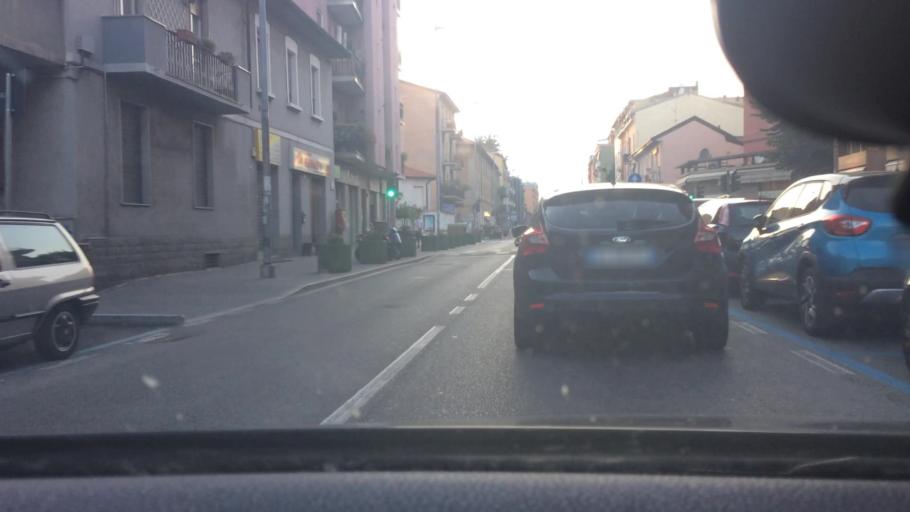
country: IT
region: Lombardy
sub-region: Citta metropolitana di Milano
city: Pero
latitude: 45.5095
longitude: 9.0888
